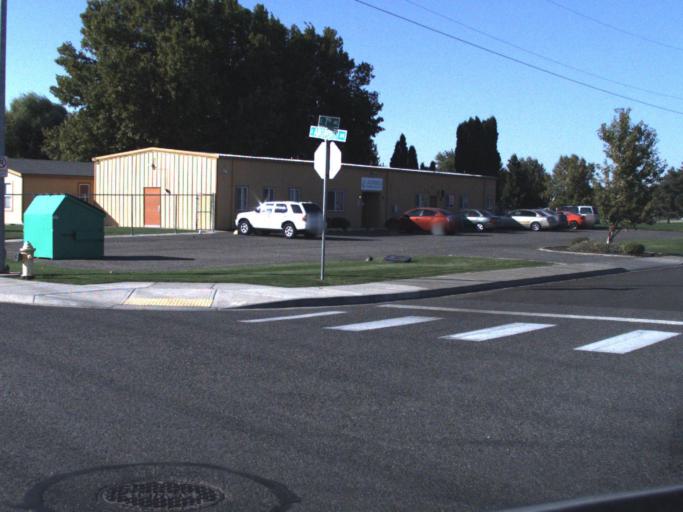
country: US
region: Washington
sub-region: Franklin County
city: Pasco
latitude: 46.2228
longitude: -119.0962
